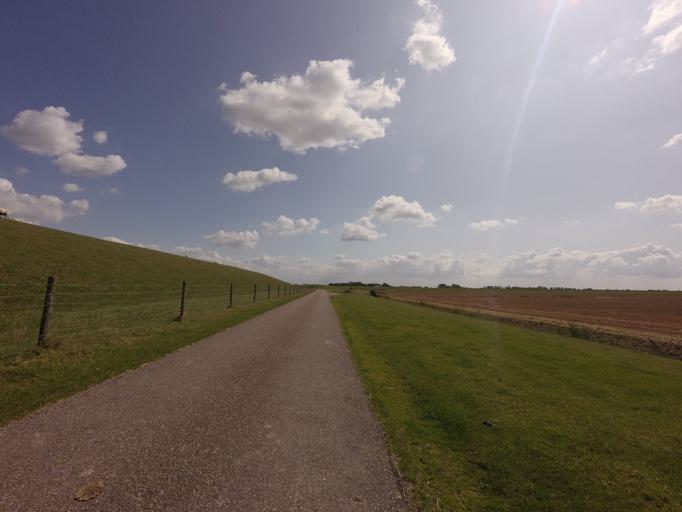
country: NL
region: Friesland
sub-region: Gemeente Ferwerderadiel
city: Hallum
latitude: 53.3200
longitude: 5.7508
